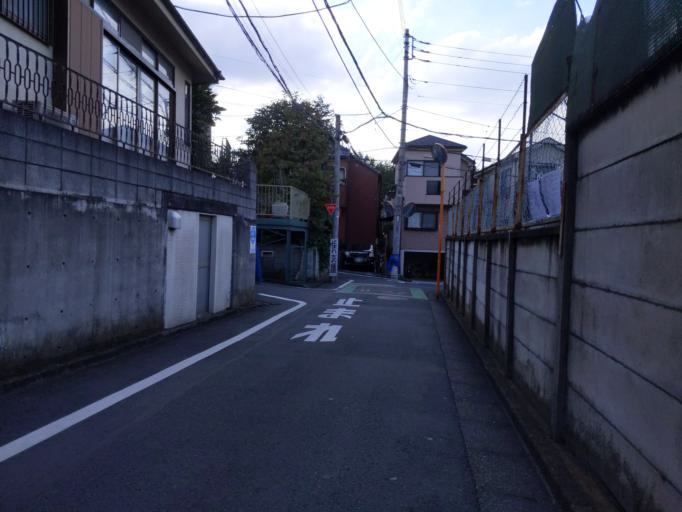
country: JP
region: Saitama
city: Wako
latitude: 35.7437
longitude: 139.6421
